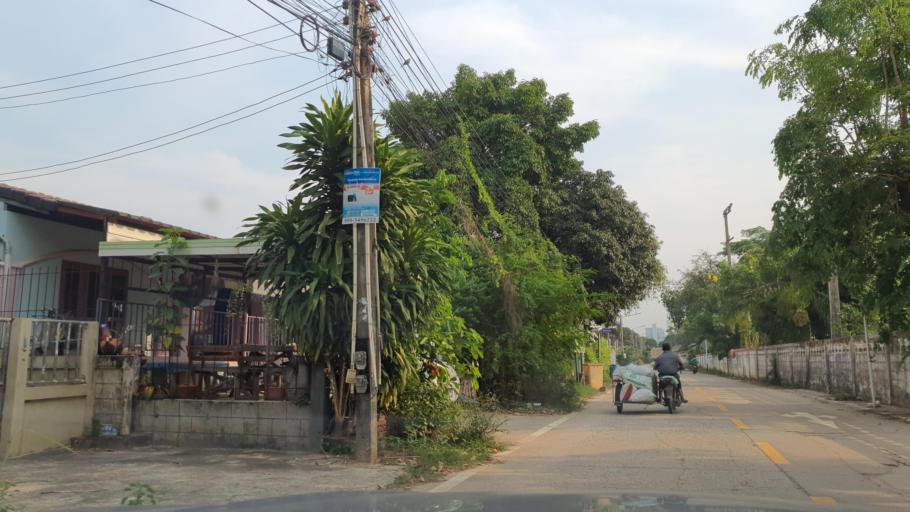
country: TH
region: Rayong
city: Rayong
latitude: 12.6199
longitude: 101.4032
